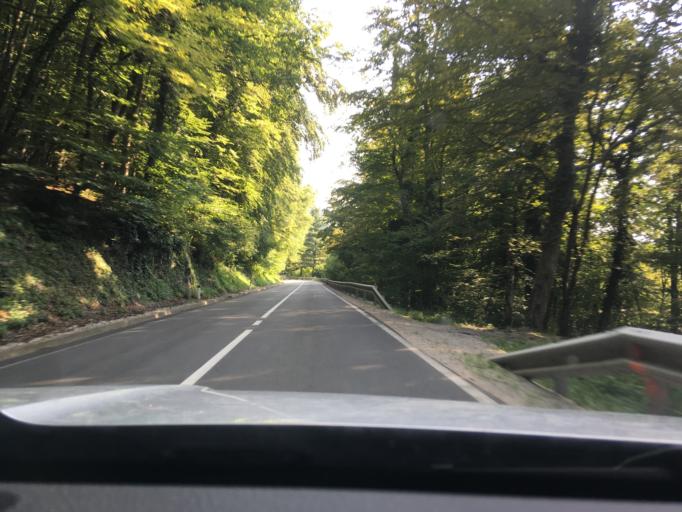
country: SI
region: Novo Mesto
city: Novo Mesto
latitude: 45.7319
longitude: 15.2198
